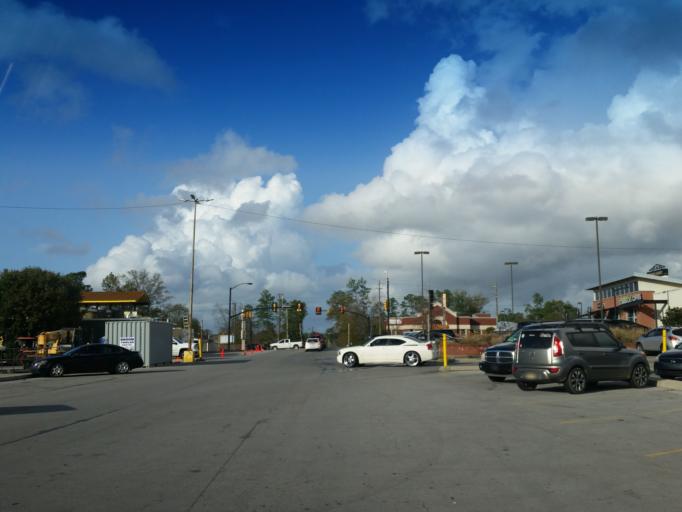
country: US
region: Mississippi
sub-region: Lamar County
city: West Hattiesburg
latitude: 31.3238
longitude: -89.3455
